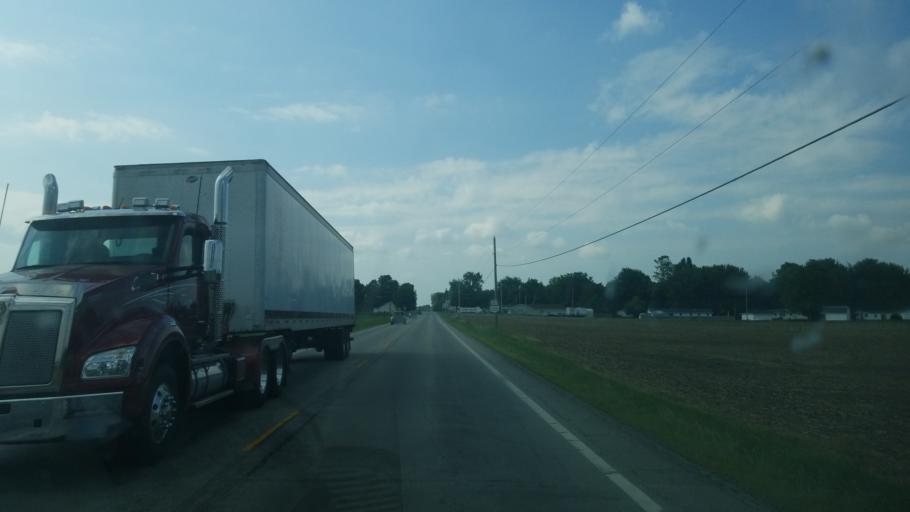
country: US
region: Ohio
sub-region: Logan County
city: Russells Point
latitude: 40.5215
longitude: -83.8274
